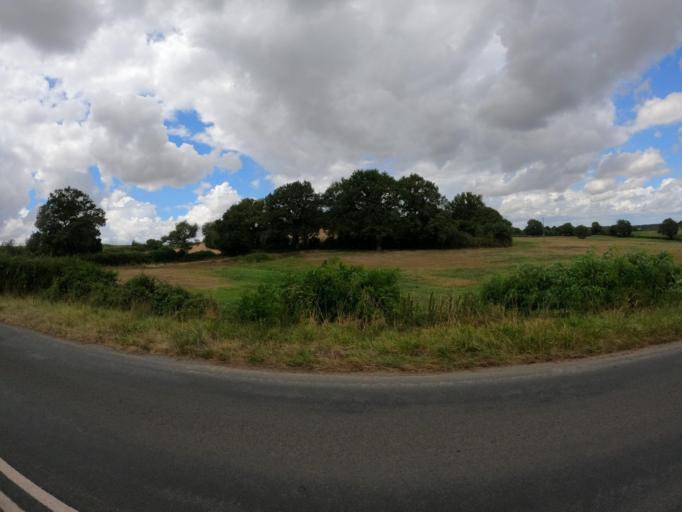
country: FR
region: Pays de la Loire
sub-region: Departement de Maine-et-Loire
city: Morannes
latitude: 47.8107
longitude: -0.4140
